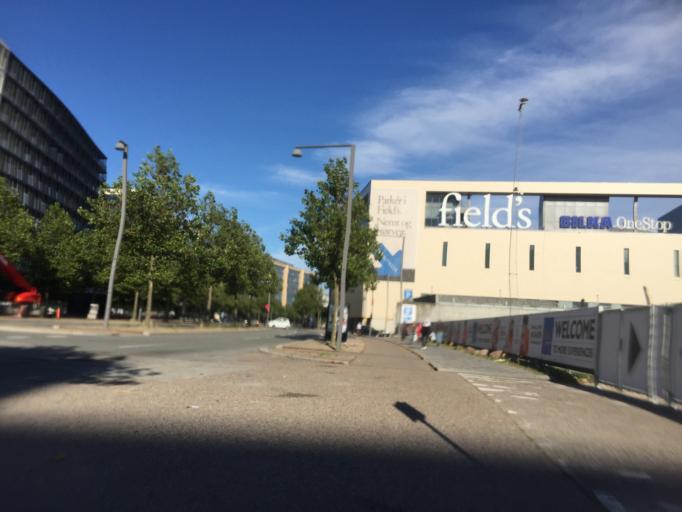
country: DK
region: Capital Region
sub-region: Tarnby Kommune
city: Tarnby
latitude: 55.6312
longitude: 12.5742
